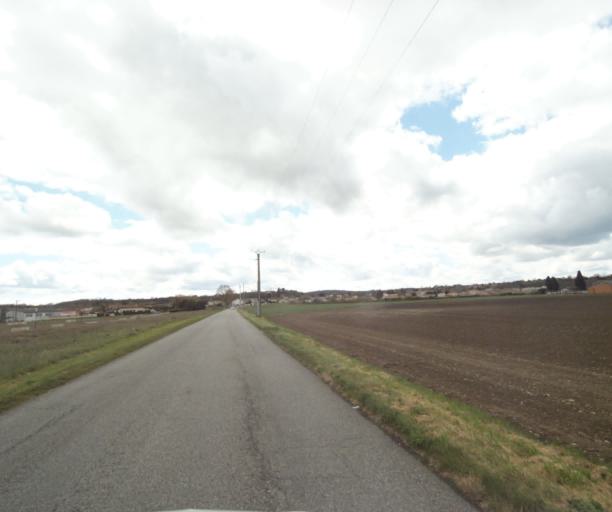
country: FR
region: Midi-Pyrenees
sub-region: Departement de l'Ariege
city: Saverdun
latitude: 43.2386
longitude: 1.5843
